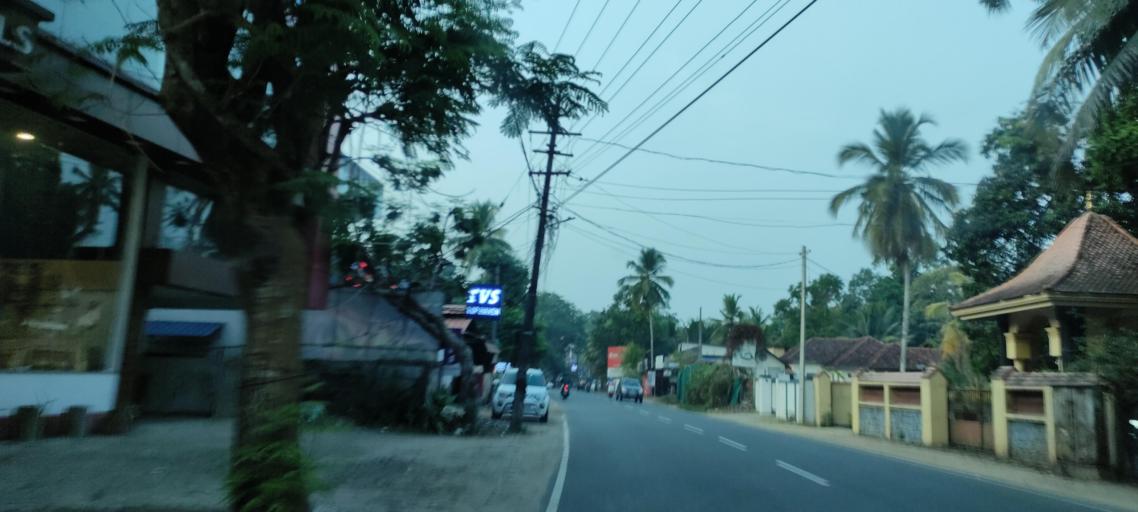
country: IN
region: Kerala
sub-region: Alappuzha
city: Mavelikara
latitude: 9.3061
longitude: 76.5343
